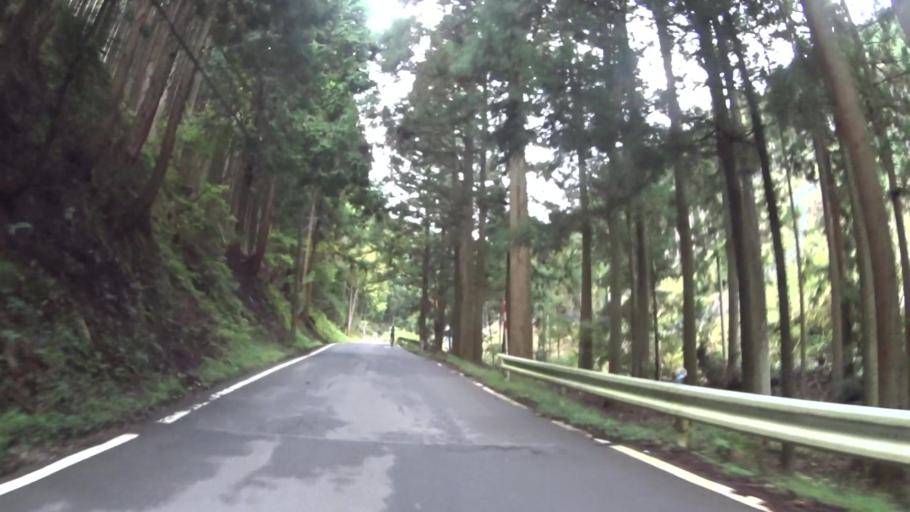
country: JP
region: Kyoto
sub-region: Kyoto-shi
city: Kamigyo-ku
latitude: 35.1453
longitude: 135.7831
